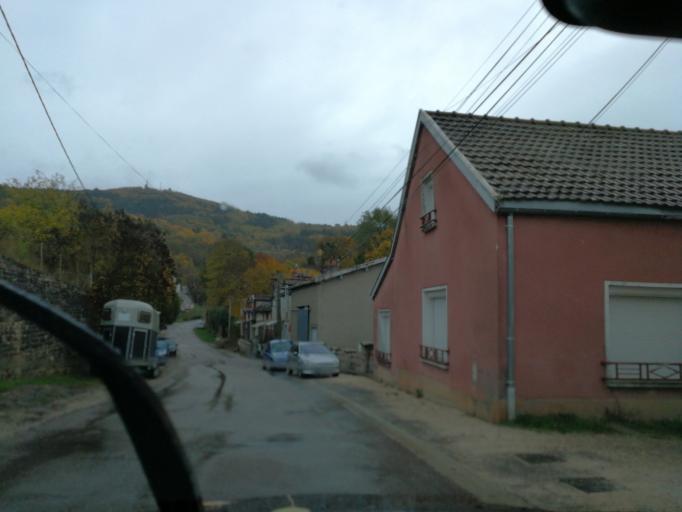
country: FR
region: Bourgogne
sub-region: Departement de la Cote-d'Or
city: Fleurey-sur-Ouche
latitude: 47.3258
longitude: 4.8003
